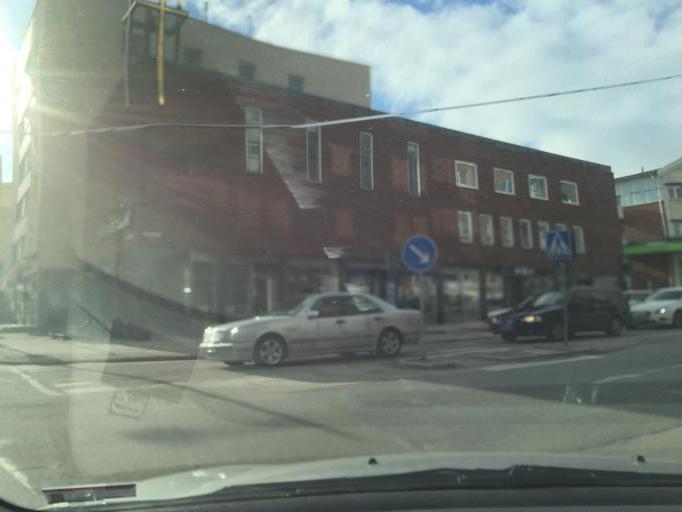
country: SE
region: Norrbotten
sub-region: Lulea Kommun
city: Lulea
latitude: 65.5857
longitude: 22.1561
